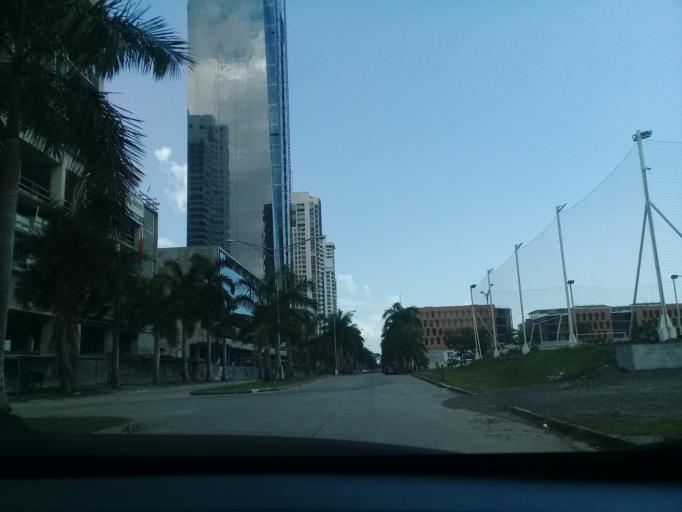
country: PA
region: Panama
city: San Miguelito
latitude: 9.0154
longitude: -79.4684
